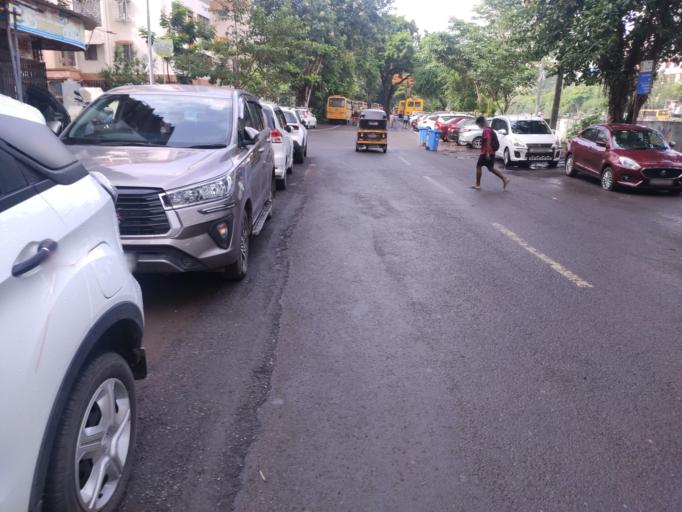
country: IN
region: Maharashtra
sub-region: Mumbai Suburban
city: Borivli
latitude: 19.2450
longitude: 72.8573
